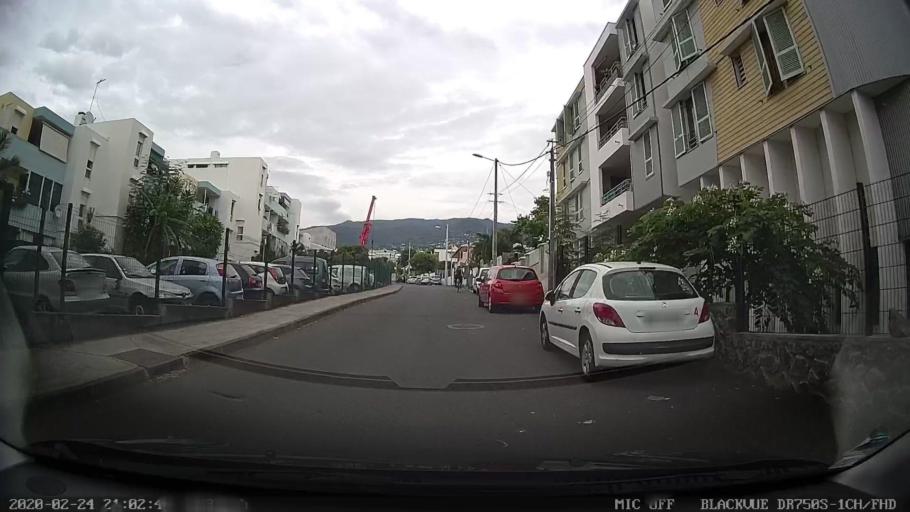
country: RE
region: Reunion
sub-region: Reunion
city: Saint-Denis
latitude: -20.8960
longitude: 55.4838
